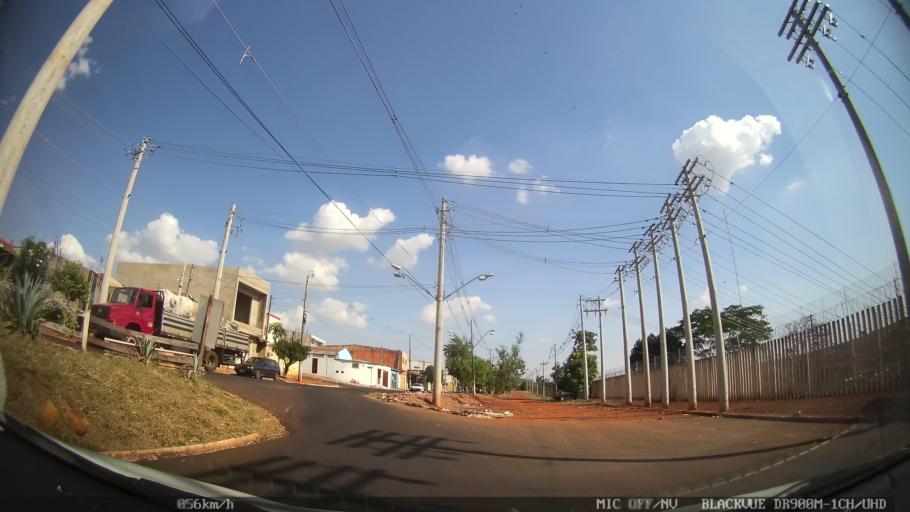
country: BR
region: Sao Paulo
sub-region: Ribeirao Preto
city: Ribeirao Preto
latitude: -21.1981
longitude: -47.8537
